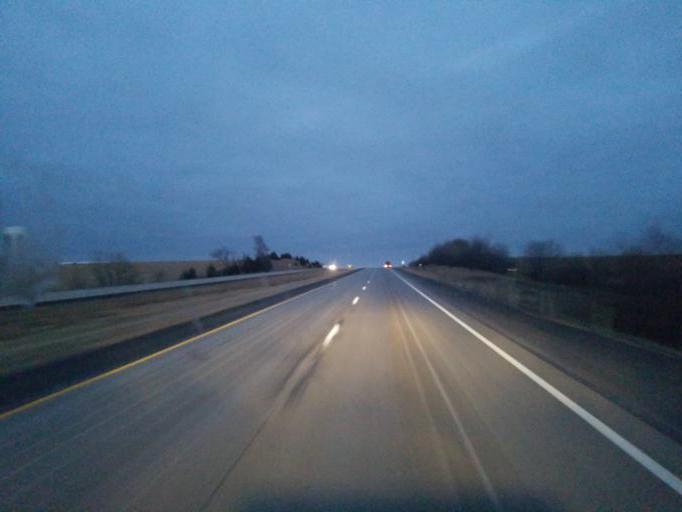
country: US
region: Iowa
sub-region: Cass County
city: Atlantic
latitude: 41.4971
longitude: -94.9206
